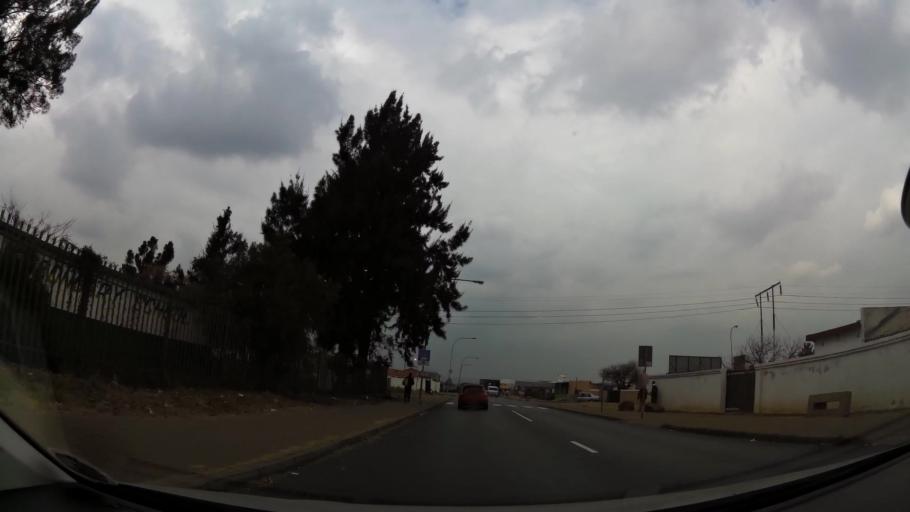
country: ZA
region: Gauteng
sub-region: City of Johannesburg Metropolitan Municipality
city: Soweto
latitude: -26.2591
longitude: 27.8595
